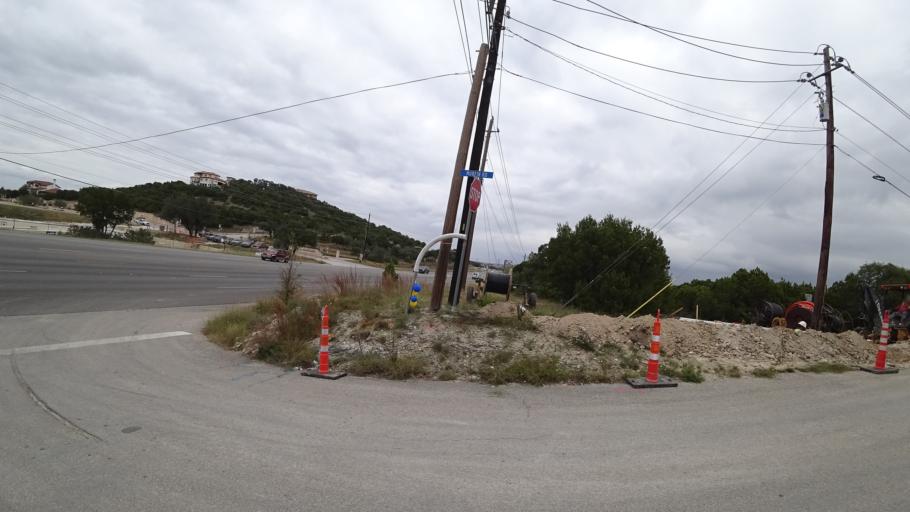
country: US
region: Texas
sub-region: Travis County
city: Lakeway
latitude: 30.3577
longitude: -97.9575
